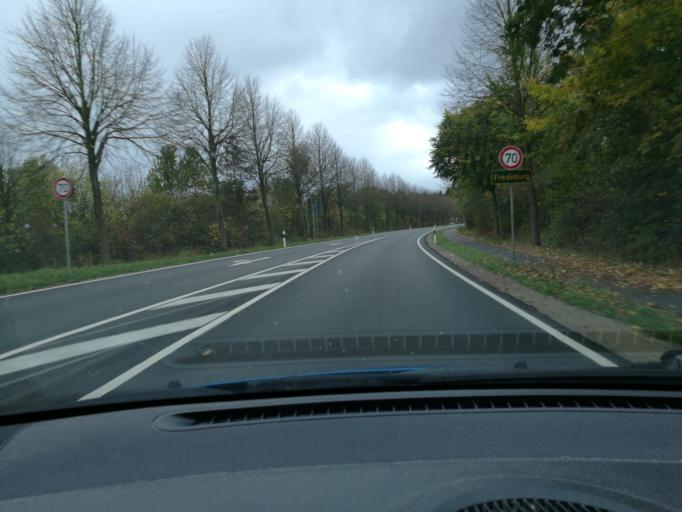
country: DE
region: Schleswig-Holstein
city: Fredeburg
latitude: 53.6754
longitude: 10.7285
